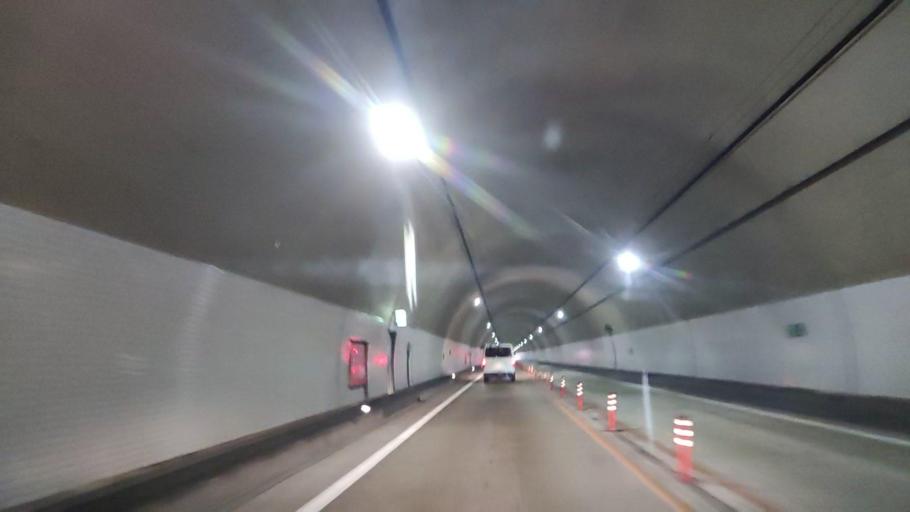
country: JP
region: Akita
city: Odate
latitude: 40.3415
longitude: 140.6414
